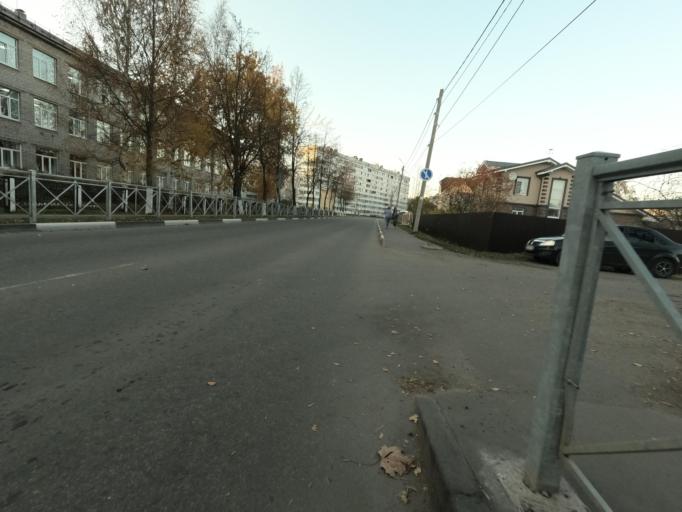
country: RU
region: Leningrad
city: Kirovsk
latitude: 59.8786
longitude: 30.9907
